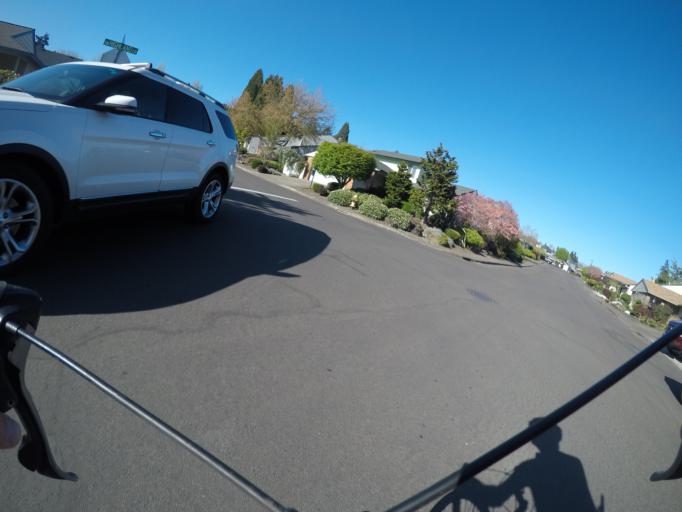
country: US
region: Oregon
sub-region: Washington County
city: King City
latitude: 45.4071
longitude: -122.7890
